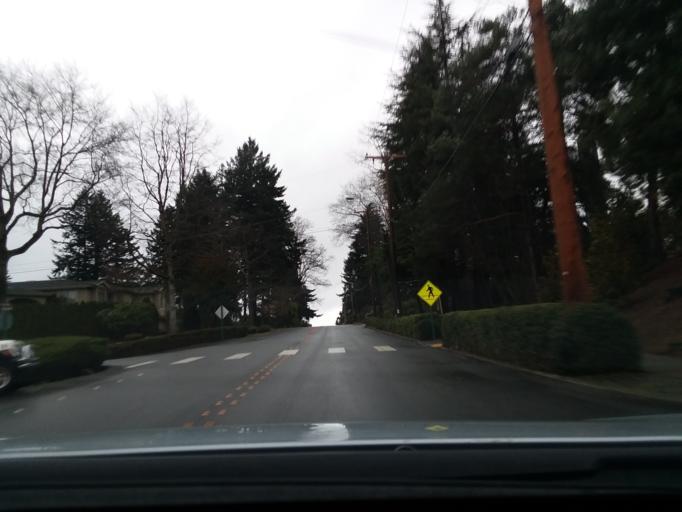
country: US
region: Washington
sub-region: King County
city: Clyde Hill
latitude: 47.6230
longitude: -122.2112
